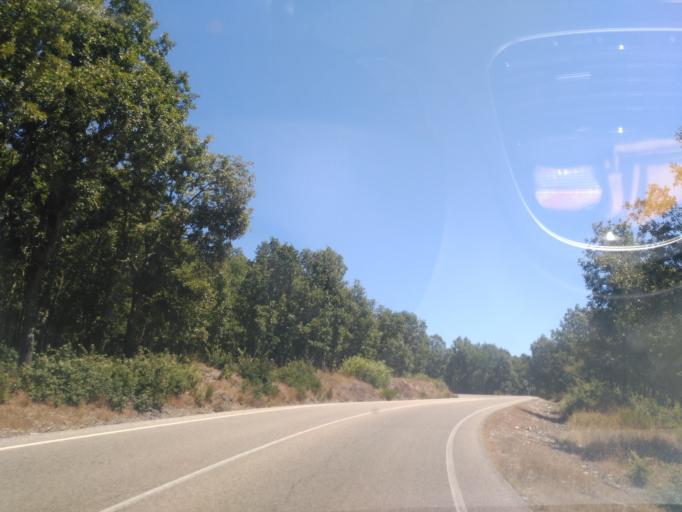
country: ES
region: Castille and Leon
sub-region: Provincia de Zamora
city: Puebla de Sanabria
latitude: 42.0804
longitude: -6.6375
